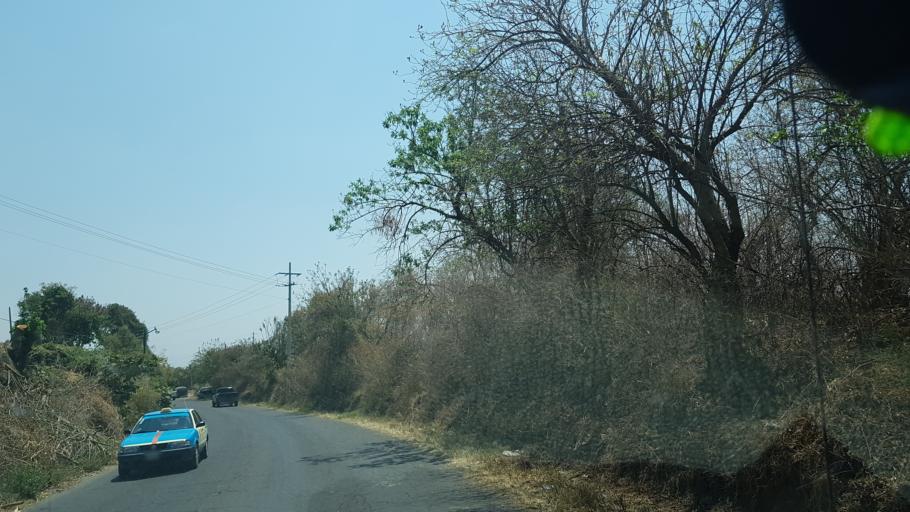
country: MX
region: Puebla
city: Tochimilco
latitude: 18.8867
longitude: -98.5532
